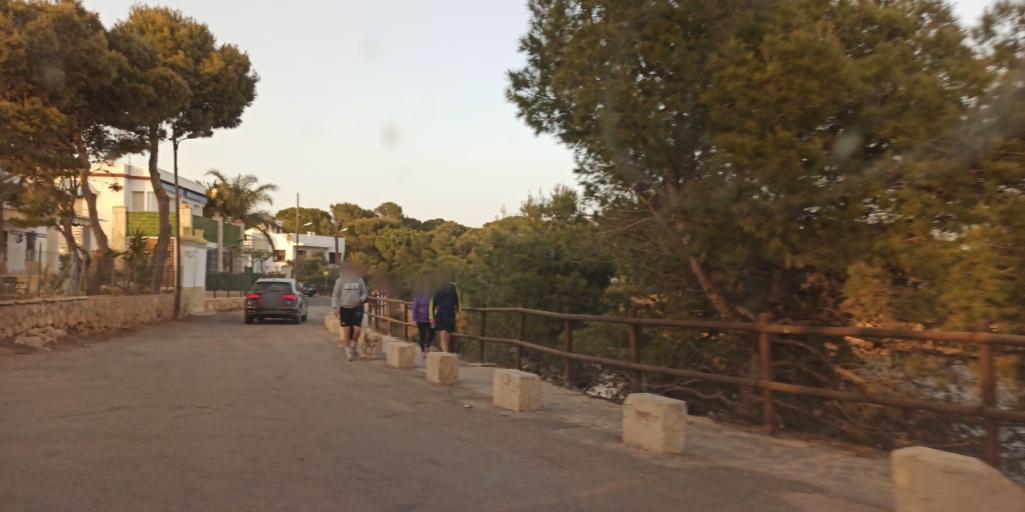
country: ES
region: Catalonia
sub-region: Provincia de Tarragona
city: L'Ampolla
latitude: 40.8131
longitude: 0.7170
